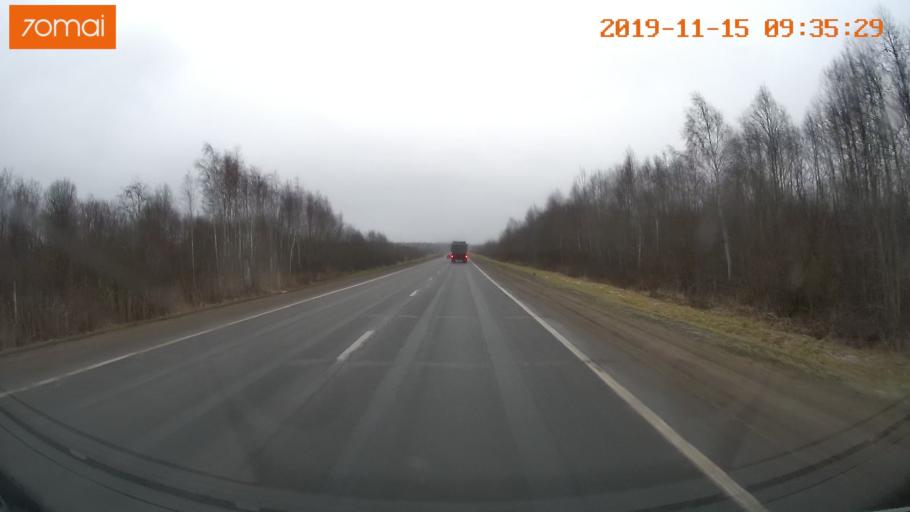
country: RU
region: Vologda
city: Sheksna
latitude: 59.2540
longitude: 38.4005
